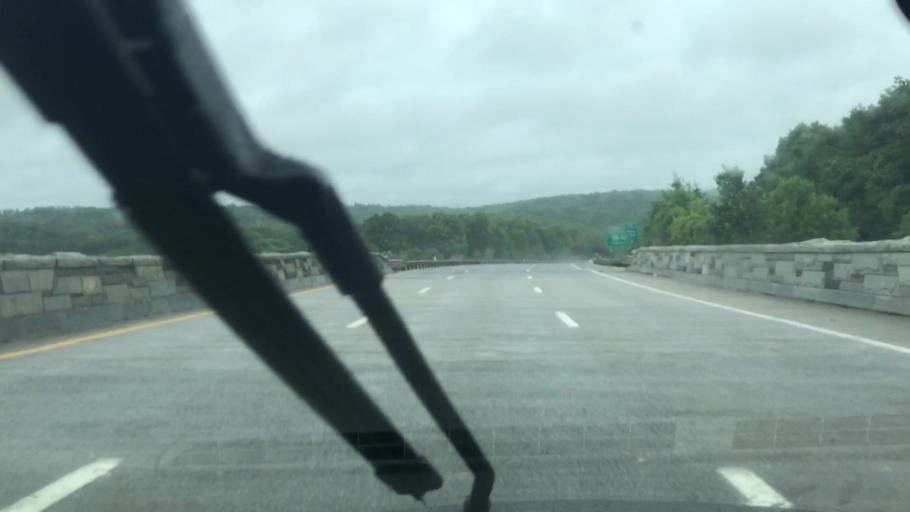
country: US
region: New York
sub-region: Westchester County
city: Jefferson Valley-Yorktown
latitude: 41.2922
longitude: -73.8213
